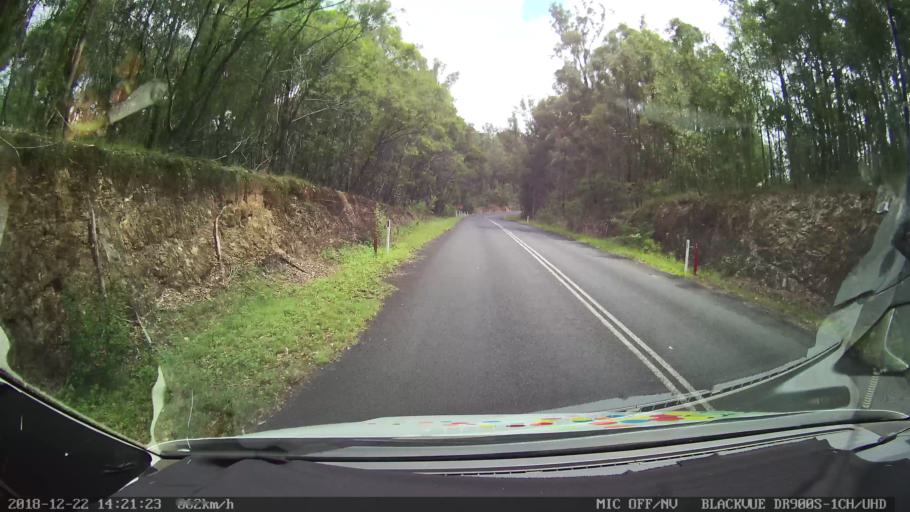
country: AU
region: New South Wales
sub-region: Clarence Valley
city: Coutts Crossing
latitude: -30.0199
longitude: 152.6589
